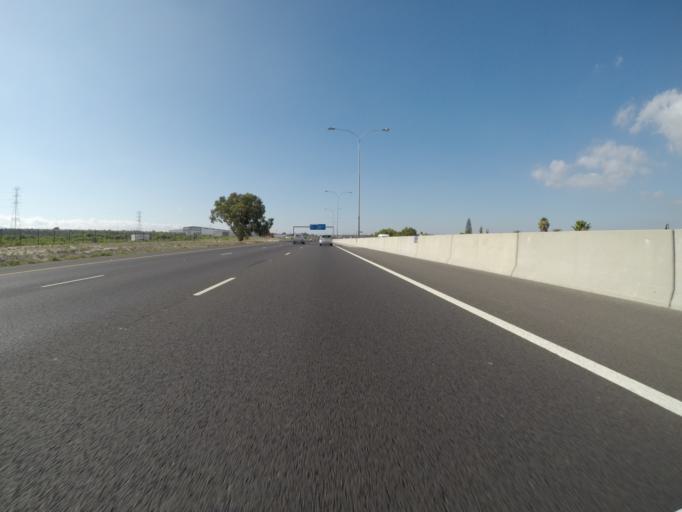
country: ZA
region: Western Cape
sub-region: City of Cape Town
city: Kraaifontein
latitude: -33.9248
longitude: 18.6633
